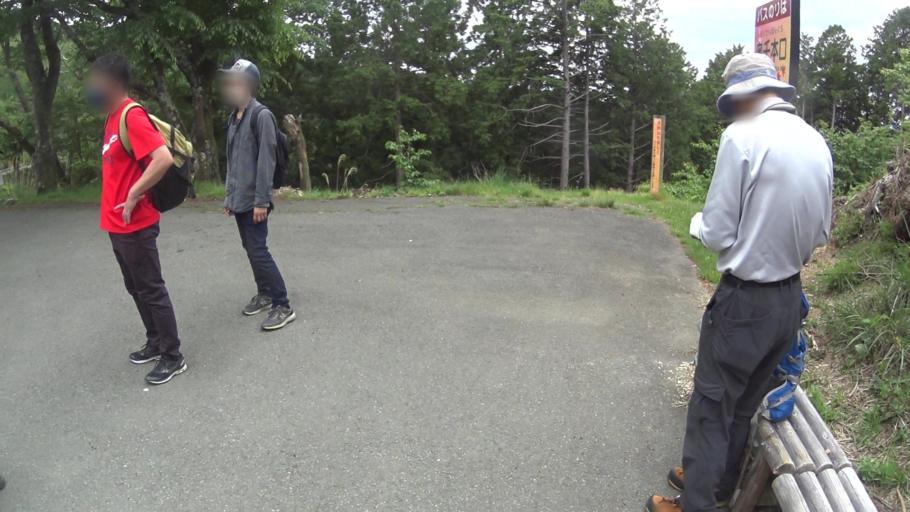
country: JP
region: Nara
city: Yoshino-cho
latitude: 34.3453
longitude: 135.8799
